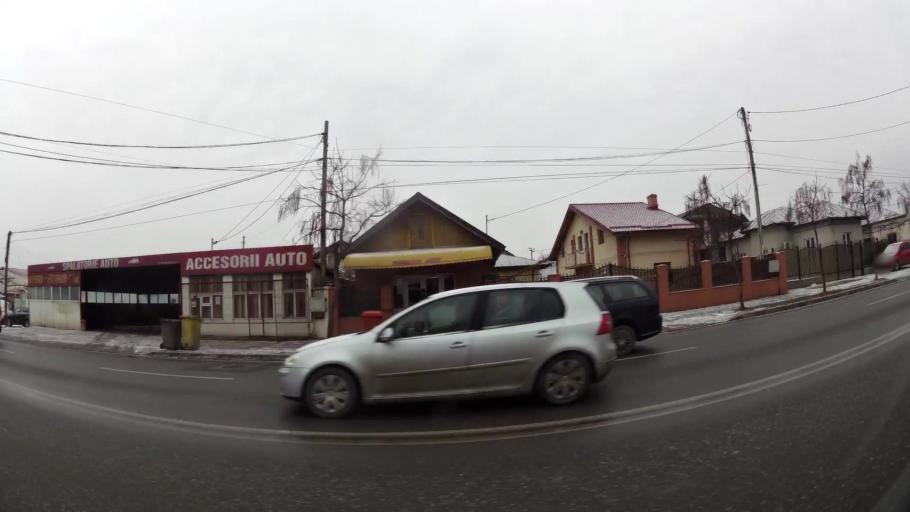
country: RO
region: Dambovita
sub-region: Comuna Ulmi
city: Ulmi
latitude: 44.9128
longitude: 25.4845
